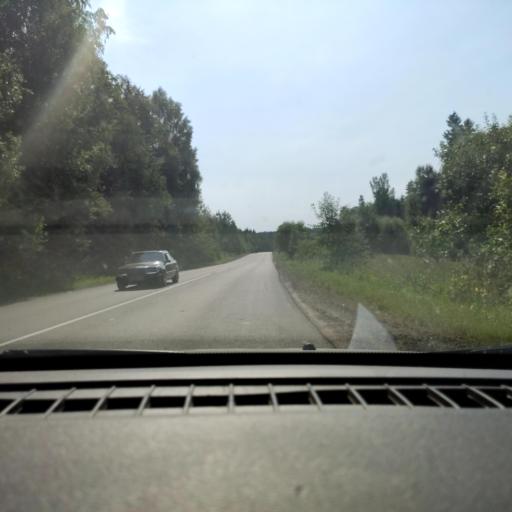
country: RU
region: Perm
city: Novyye Lyady
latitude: 58.1247
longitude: 56.4677
